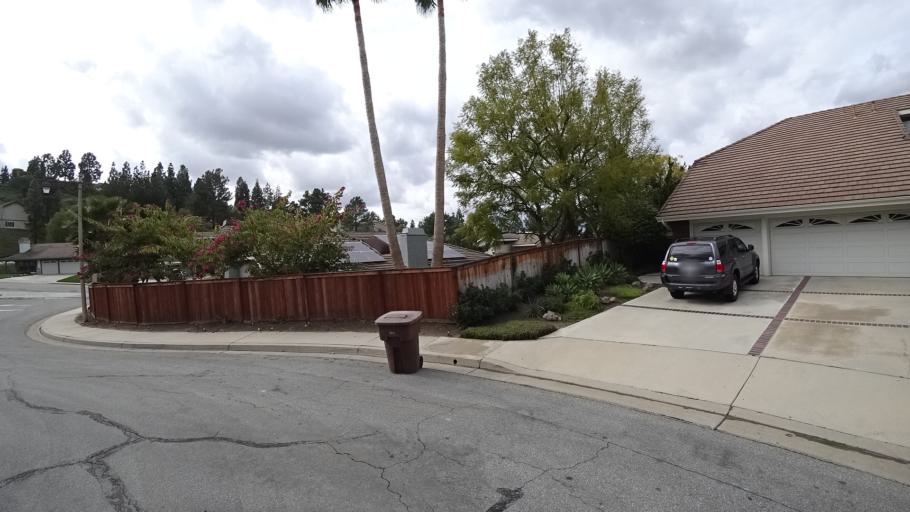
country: US
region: California
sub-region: Orange County
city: Villa Park
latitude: 33.8429
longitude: -117.7850
